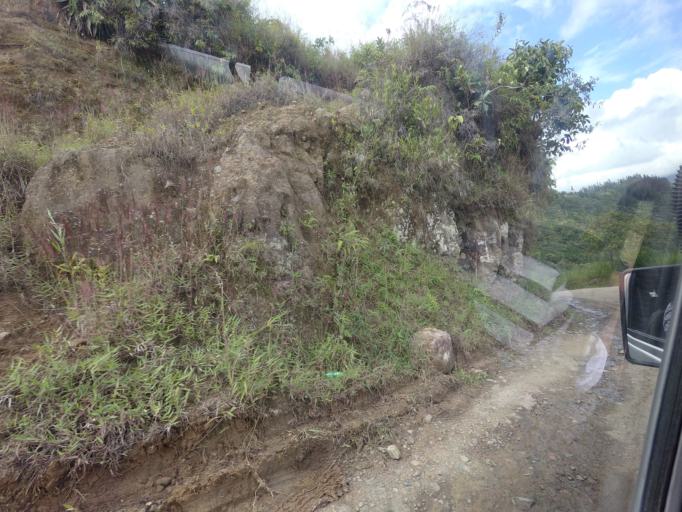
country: CO
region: Huila
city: San Agustin
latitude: 1.9229
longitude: -76.2955
